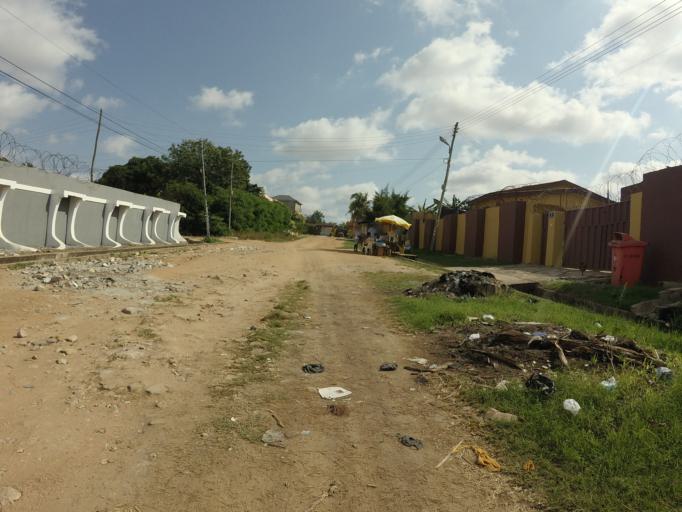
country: GH
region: Greater Accra
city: Dome
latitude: 5.6185
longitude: -0.2390
